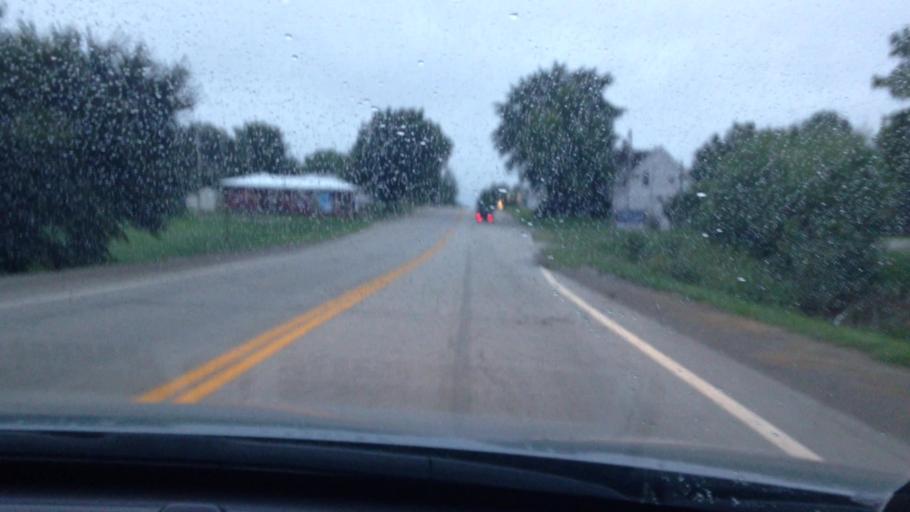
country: US
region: Kansas
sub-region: Brown County
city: Horton
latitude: 39.6736
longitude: -95.5272
